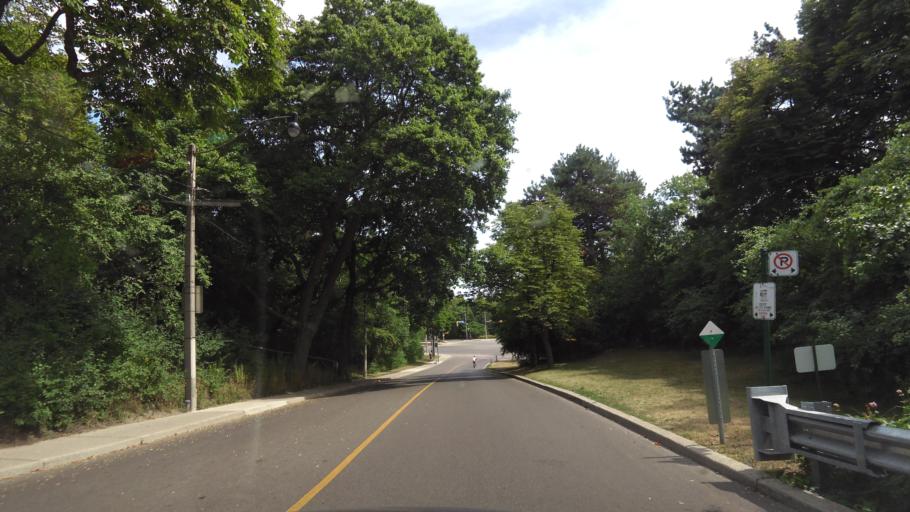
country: CA
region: Ontario
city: Toronto
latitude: 43.6403
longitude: -79.4606
